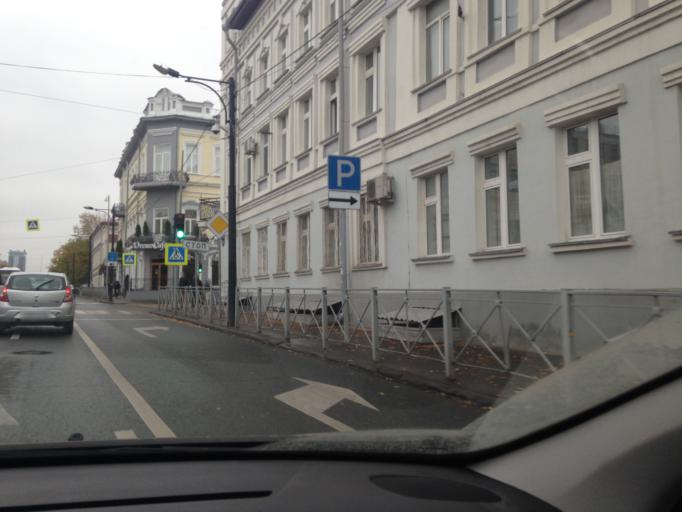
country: RU
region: Tatarstan
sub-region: Gorod Kazan'
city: Kazan
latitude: 55.7958
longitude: 49.1291
